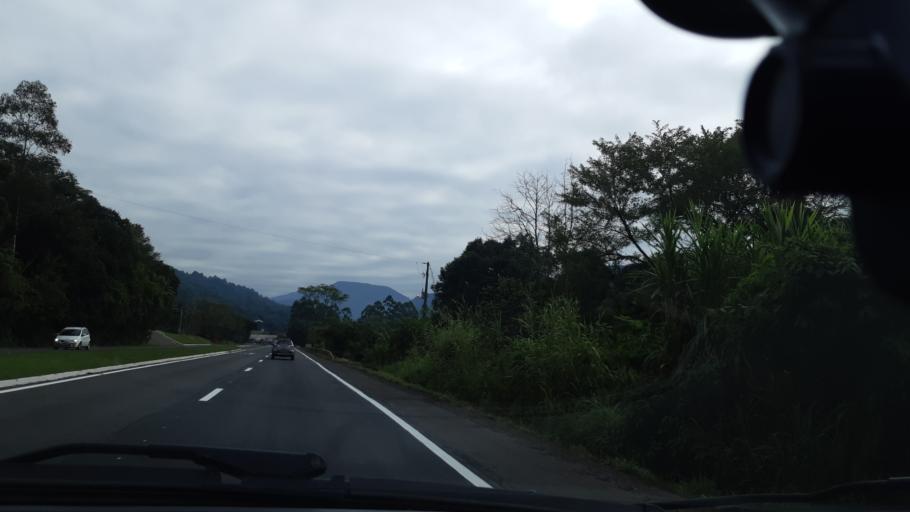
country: BR
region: Rio Grande do Sul
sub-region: Farroupilha
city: Farroupilha
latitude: -29.4050
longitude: -51.3536
